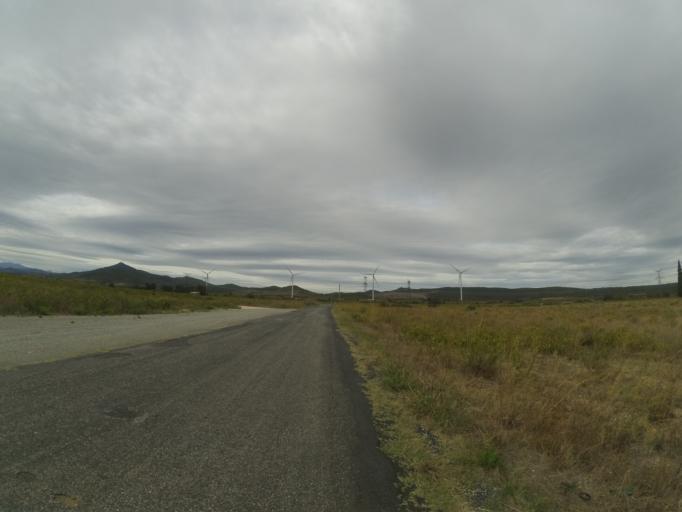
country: FR
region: Languedoc-Roussillon
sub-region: Departement des Pyrenees-Orientales
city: Pezilla-la-Riviere
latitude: 42.7161
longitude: 2.7520
